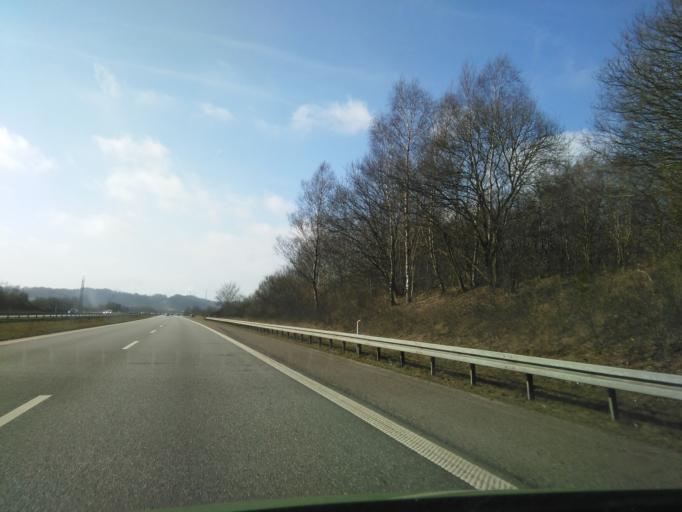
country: DK
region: Central Jutland
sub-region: Skanderborg Kommune
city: Stilling
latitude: 56.0663
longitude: 9.9761
